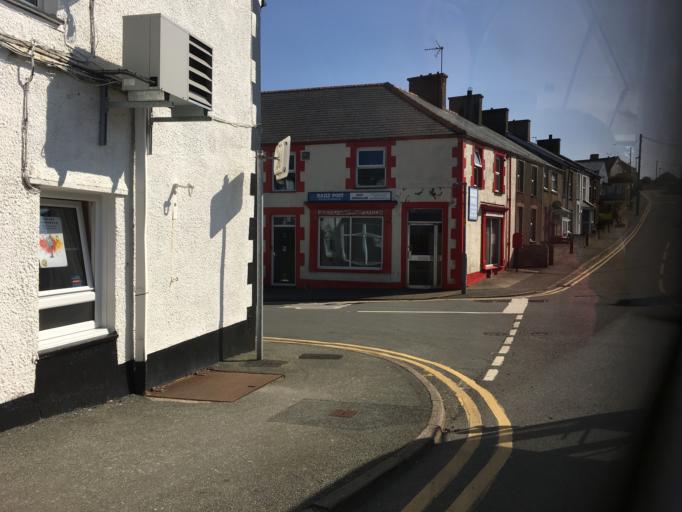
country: GB
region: Wales
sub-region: Gwynedd
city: Llanwnda
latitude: 53.0789
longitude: -4.2809
